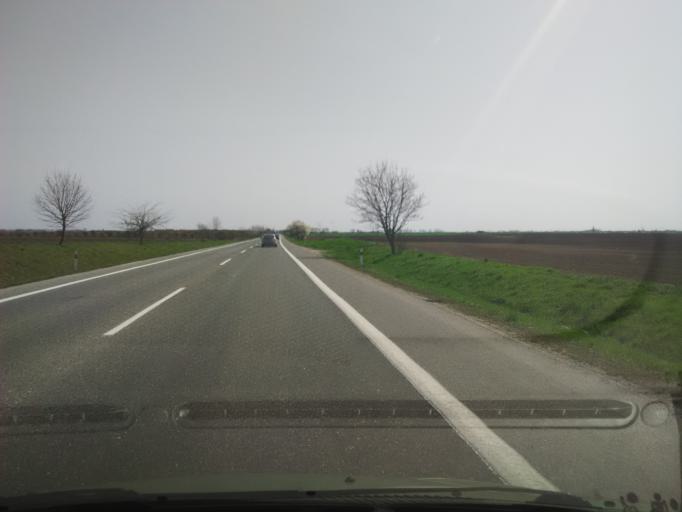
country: SK
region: Nitriansky
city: Surany
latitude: 48.1206
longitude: 18.0342
